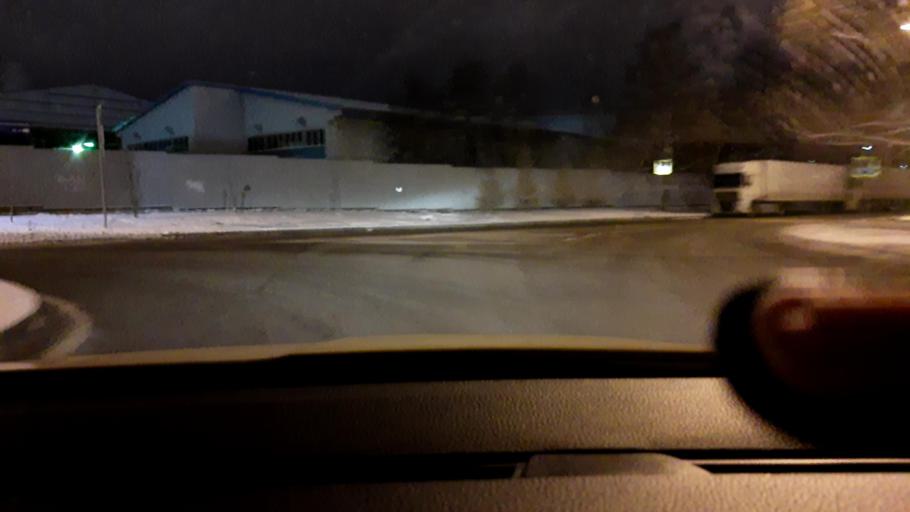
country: RU
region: Moskovskaya
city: Odintsovo
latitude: 55.6732
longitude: 37.2994
